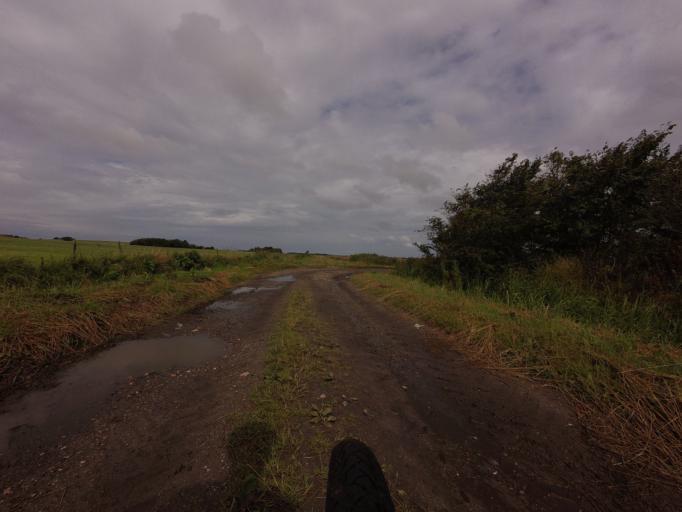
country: DK
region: North Denmark
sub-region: Jammerbugt Kommune
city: Pandrup
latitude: 57.3145
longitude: 9.7442
